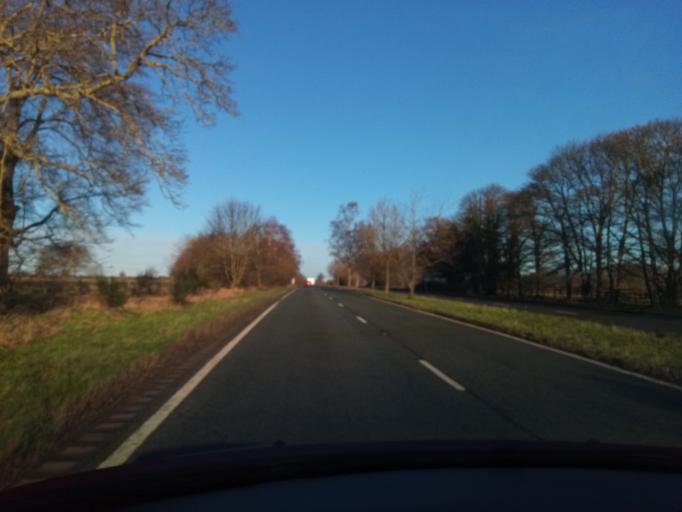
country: GB
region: England
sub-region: Nottinghamshire
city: Farnsfield
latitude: 53.0588
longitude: -1.0701
